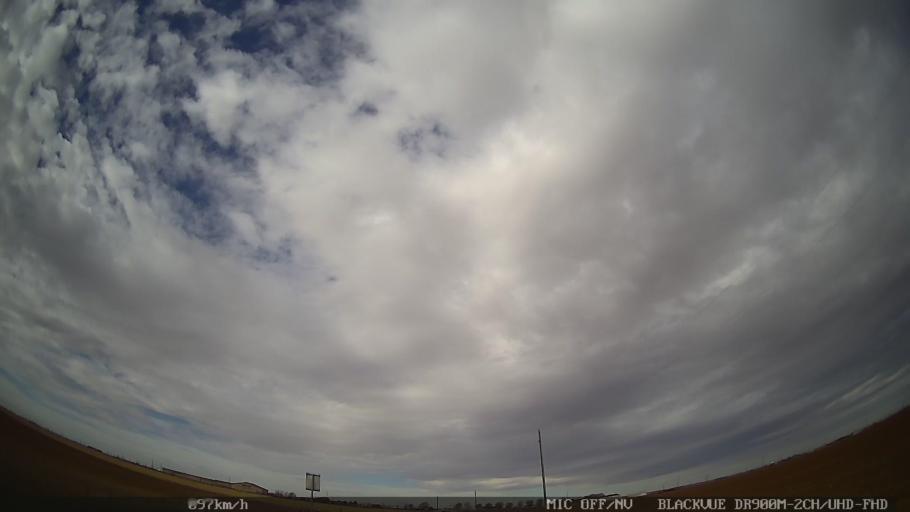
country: US
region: New Mexico
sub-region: Curry County
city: Clovis
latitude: 34.4194
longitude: -103.1294
